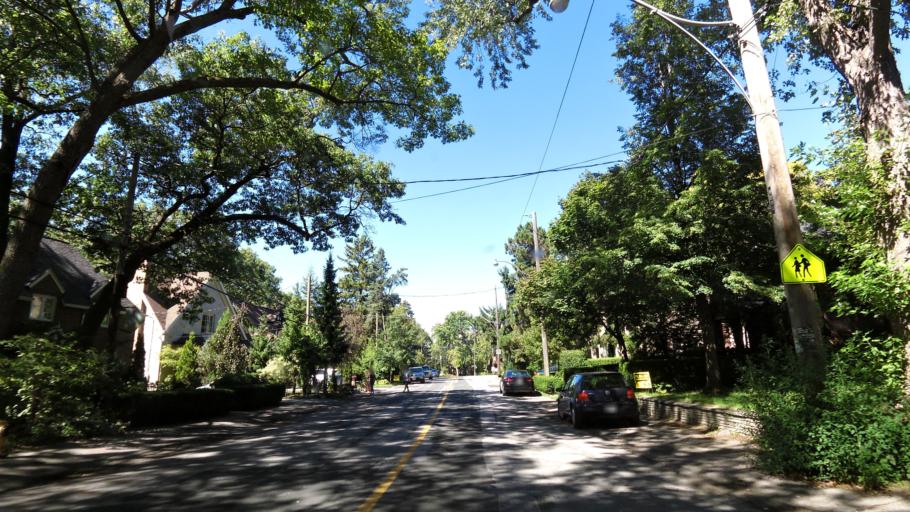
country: CA
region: Ontario
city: Etobicoke
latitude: 43.6459
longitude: -79.4852
